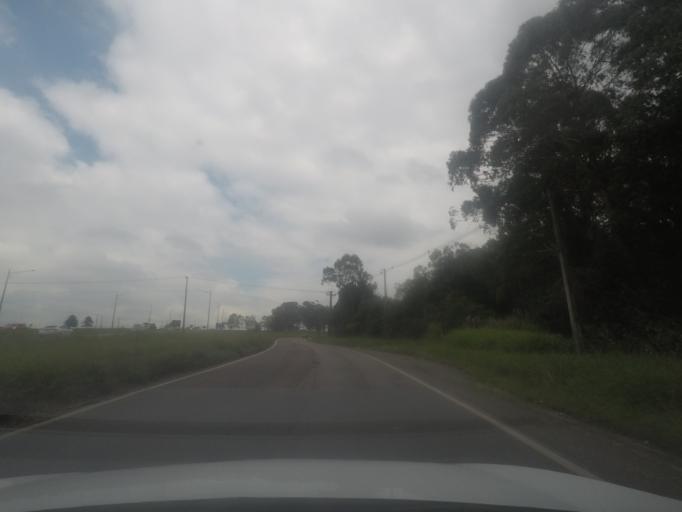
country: BR
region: Parana
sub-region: Sao Jose Dos Pinhais
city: Sao Jose dos Pinhais
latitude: -25.5402
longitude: -49.3026
